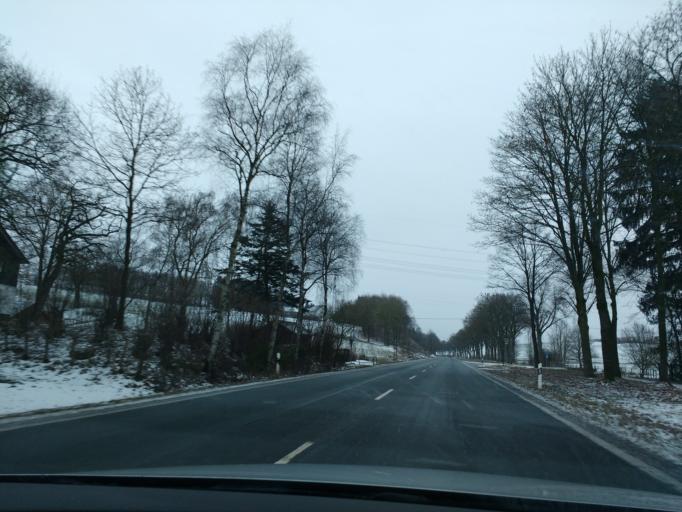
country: DE
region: North Rhine-Westphalia
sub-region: Regierungsbezirk Arnsberg
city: Brilon
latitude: 51.4304
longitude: 8.5739
